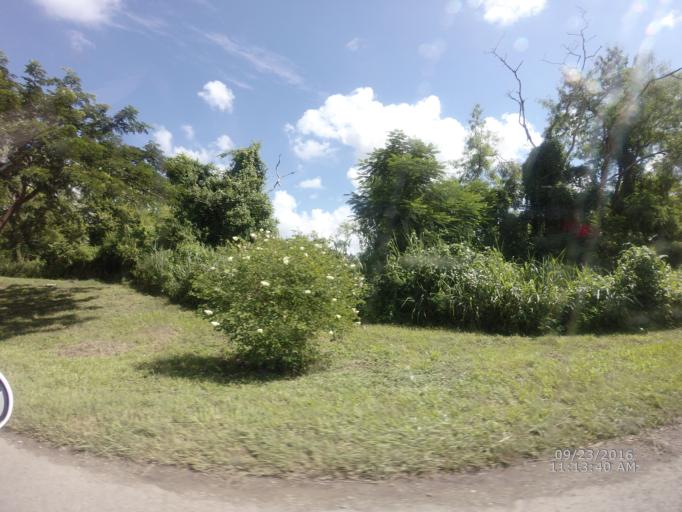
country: CU
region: La Habana
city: Arroyo Naranjo
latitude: 23.0310
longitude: -82.2991
